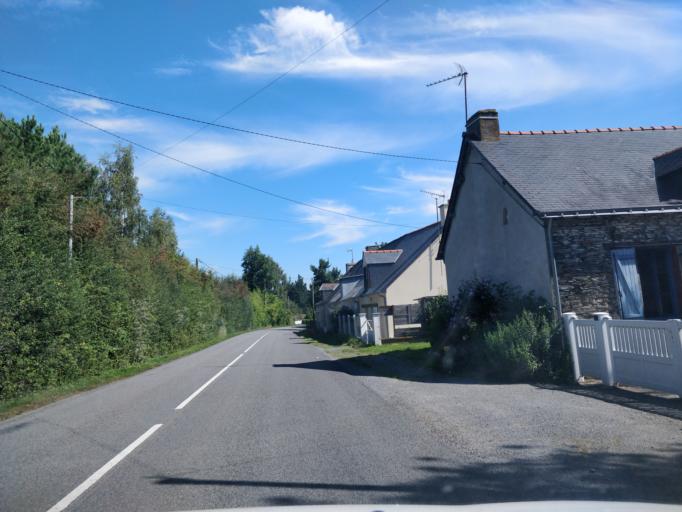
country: FR
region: Pays de la Loire
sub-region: Departement de la Loire-Atlantique
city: Conquereuil
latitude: 47.6726
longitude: -1.7724
